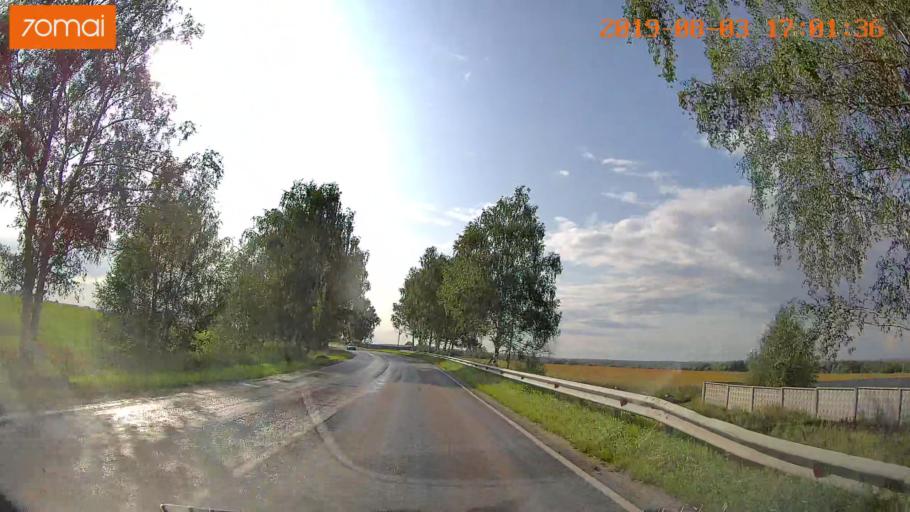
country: RU
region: Moskovskaya
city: Voskresensk
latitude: 55.3465
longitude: 38.6000
